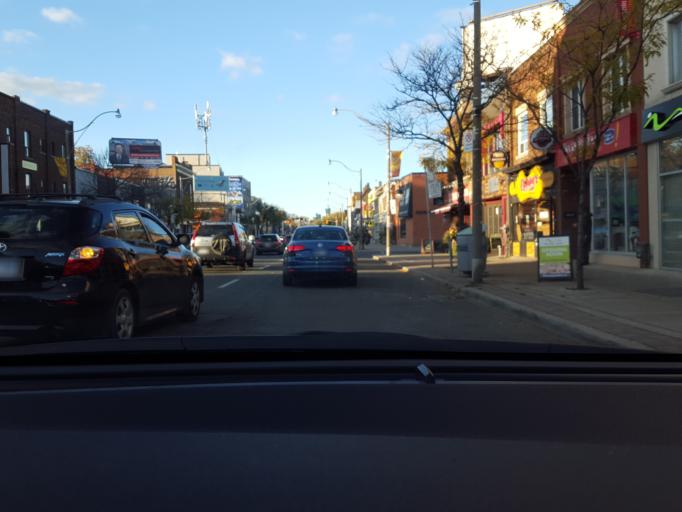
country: CA
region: Ontario
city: Toronto
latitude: 43.7290
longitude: -79.4032
